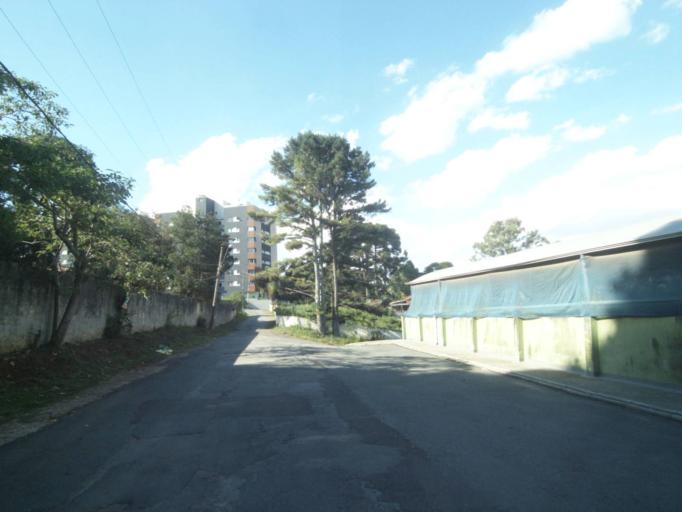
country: BR
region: Parana
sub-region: Curitiba
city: Curitiba
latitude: -25.4425
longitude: -49.3203
